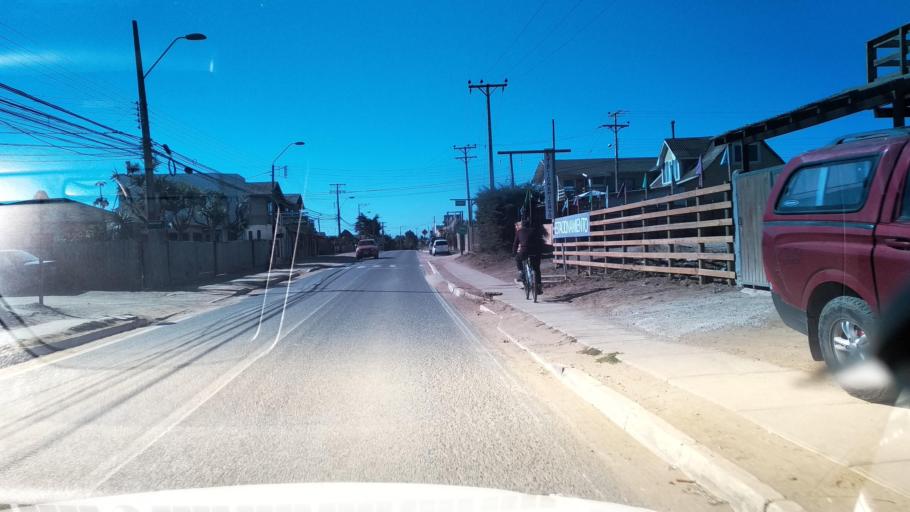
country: CL
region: O'Higgins
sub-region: Provincia de Colchagua
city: Santa Cruz
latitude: -34.4021
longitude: -72.0242
